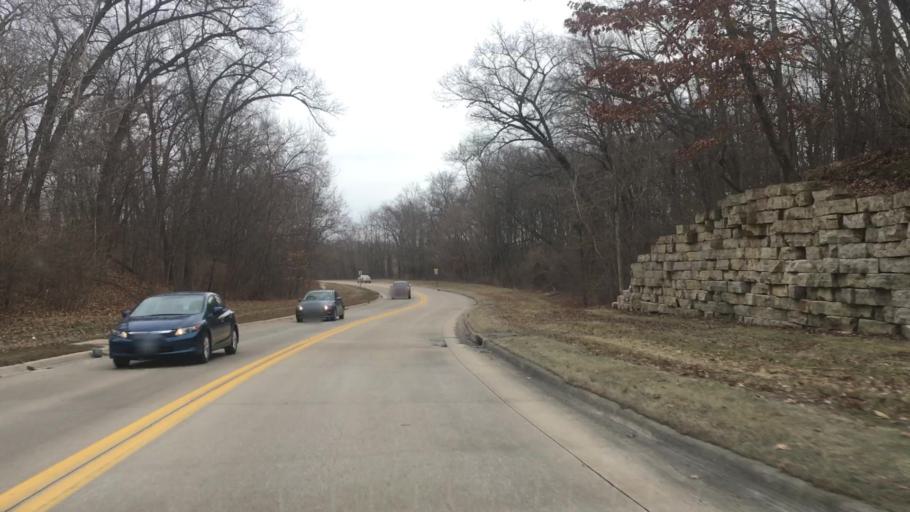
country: US
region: Iowa
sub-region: Johnson County
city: Coralville
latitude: 41.7049
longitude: -91.5789
